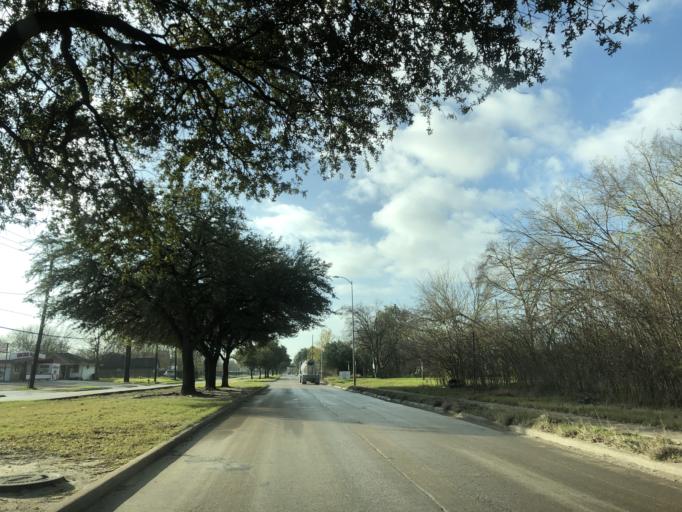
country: US
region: Texas
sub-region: Harris County
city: Jacinto City
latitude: 29.8195
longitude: -95.2846
